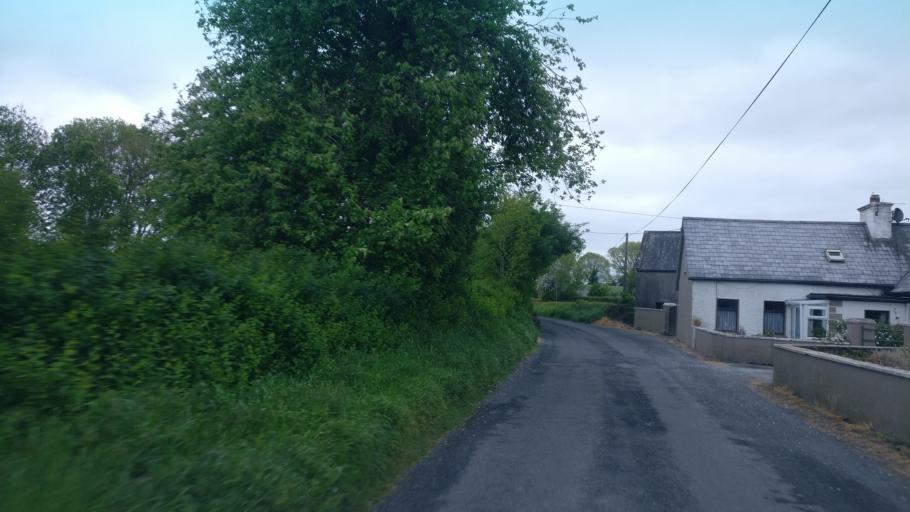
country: IE
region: Connaught
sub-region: County Galway
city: Portumna
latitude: 53.1194
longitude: -8.2896
